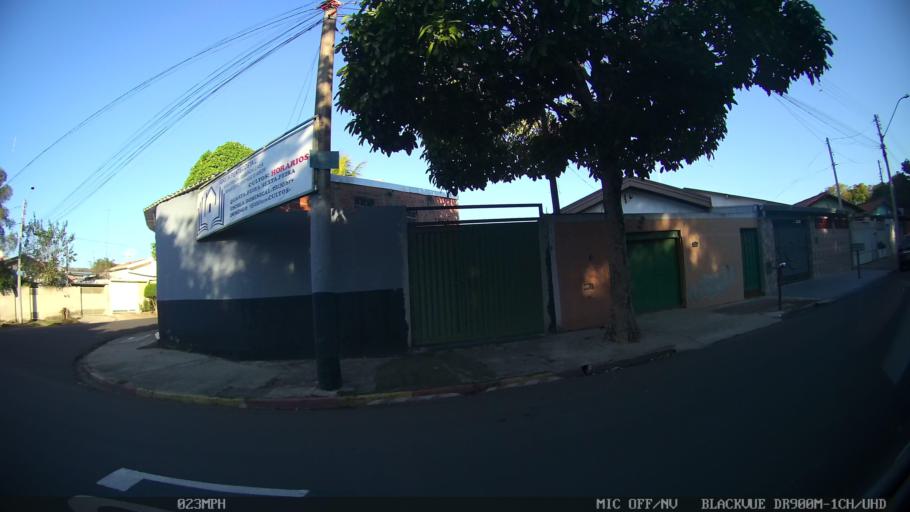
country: BR
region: Sao Paulo
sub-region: Nova Odessa
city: Nova Odessa
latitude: -22.7854
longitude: -47.2853
